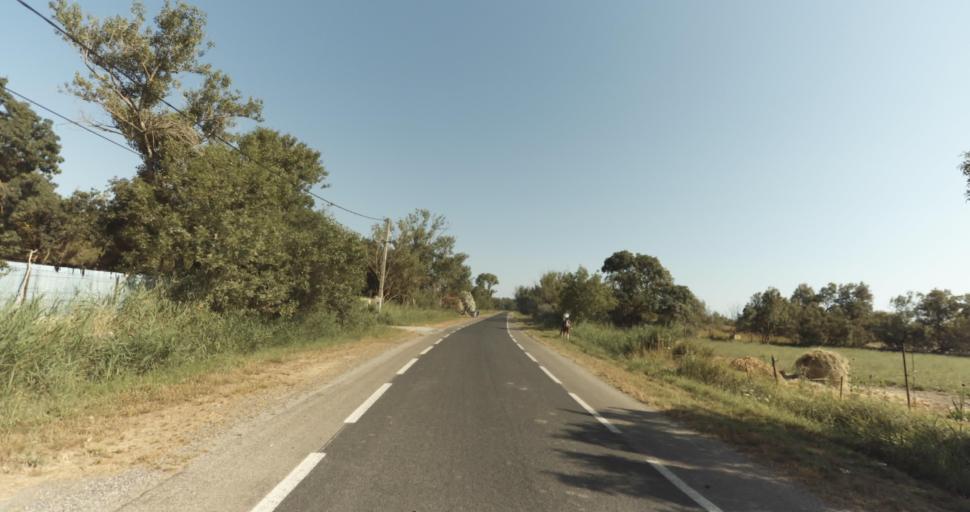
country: FR
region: Languedoc-Roussillon
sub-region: Departement des Pyrenees-Orientales
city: Saint-Cyprien-Plage
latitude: 42.6270
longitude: 3.0193
